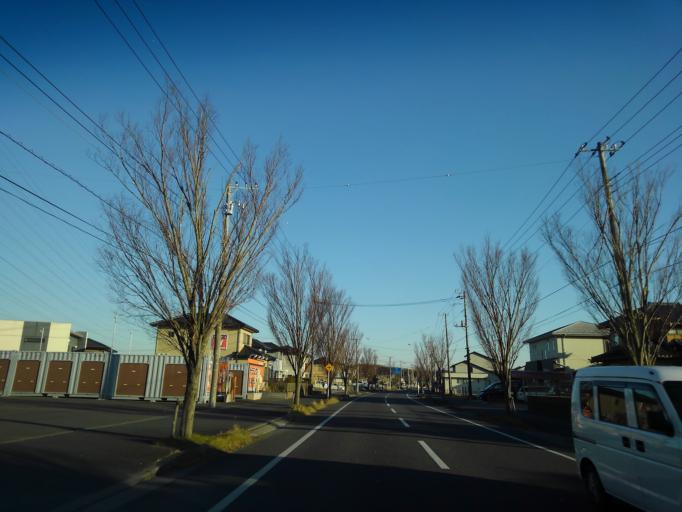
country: JP
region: Chiba
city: Kimitsu
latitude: 35.3113
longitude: 139.9196
